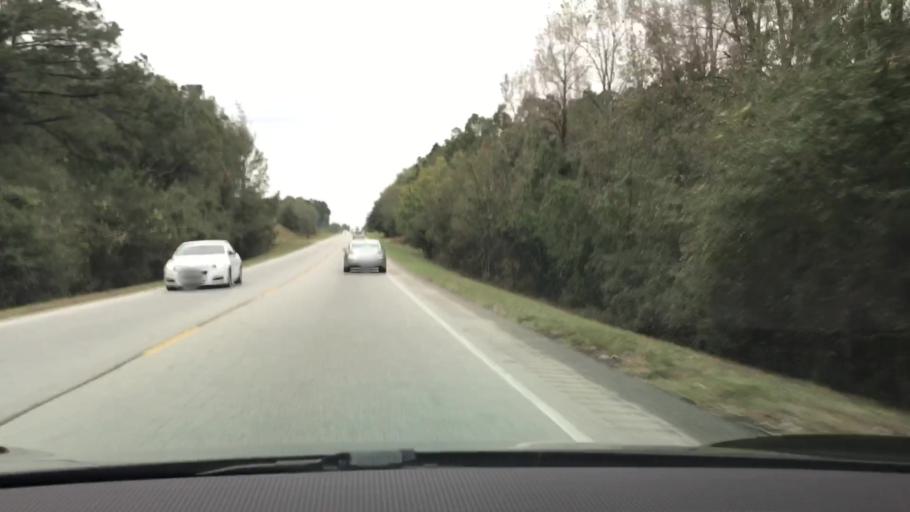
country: US
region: Georgia
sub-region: Jefferson County
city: Louisville
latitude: 32.9424
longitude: -82.3955
